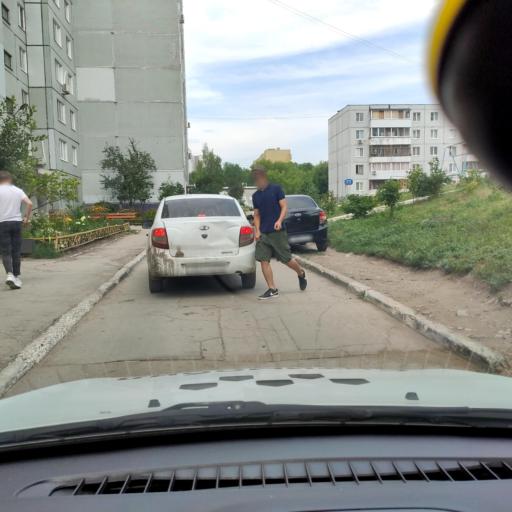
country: RU
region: Samara
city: Zhigulevsk
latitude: 53.4112
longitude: 49.5280
